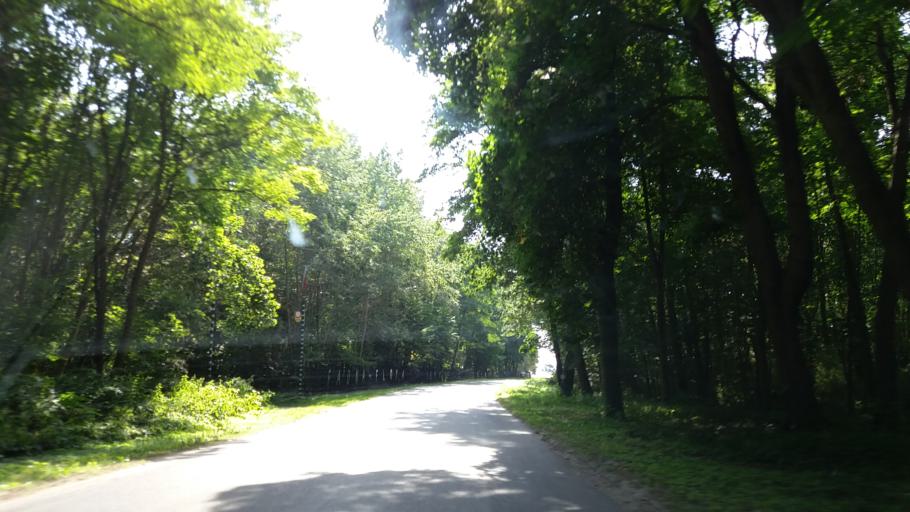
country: PL
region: West Pomeranian Voivodeship
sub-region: Powiat stargardzki
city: Stargard Szczecinski
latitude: 53.3555
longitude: 14.9721
